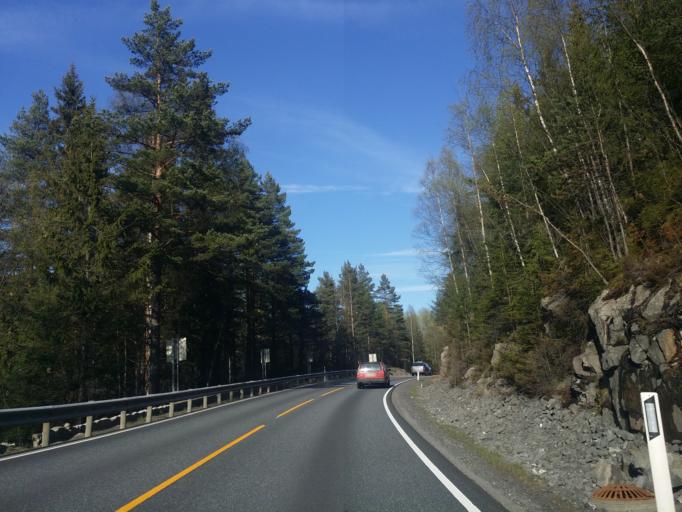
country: NO
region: Buskerud
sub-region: Kongsberg
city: Kongsberg
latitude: 59.6290
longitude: 9.5649
